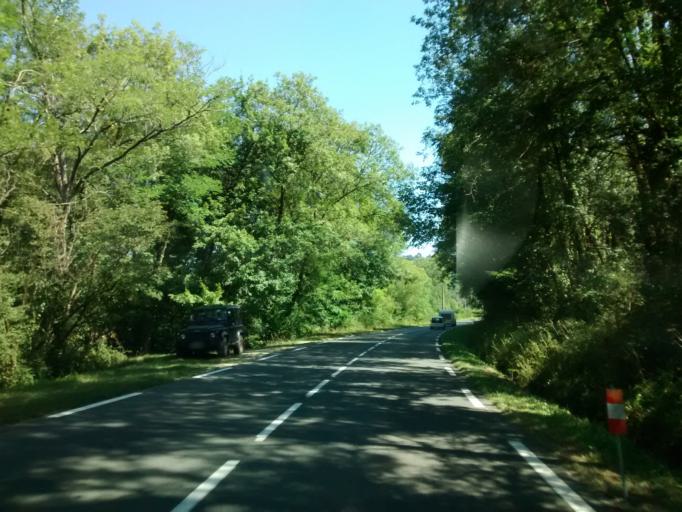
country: FR
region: Aquitaine
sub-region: Departement de la Dordogne
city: Le Bugue
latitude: 44.9566
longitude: 1.0027
